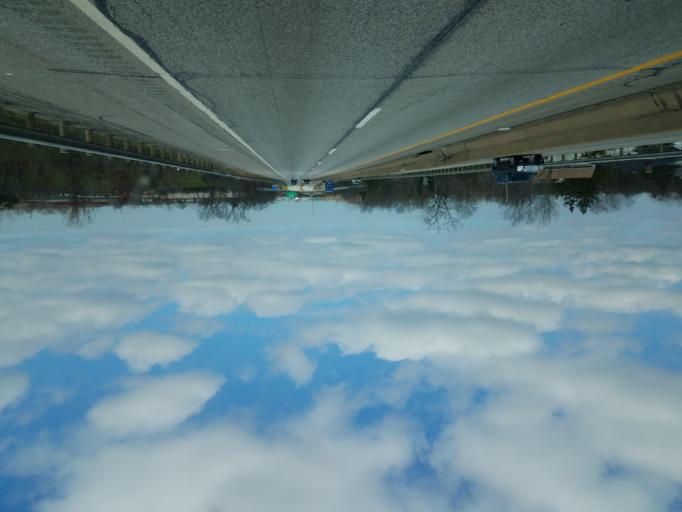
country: US
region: Ohio
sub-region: Cuyahoga County
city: Bedford Heights
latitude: 41.4115
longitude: -81.5099
